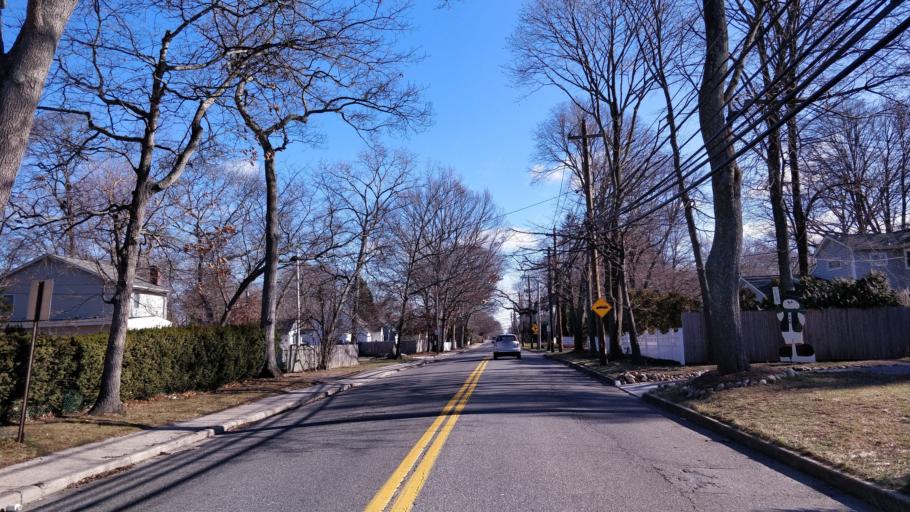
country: US
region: New York
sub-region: Suffolk County
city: Saint James
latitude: 40.8751
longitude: -73.1602
